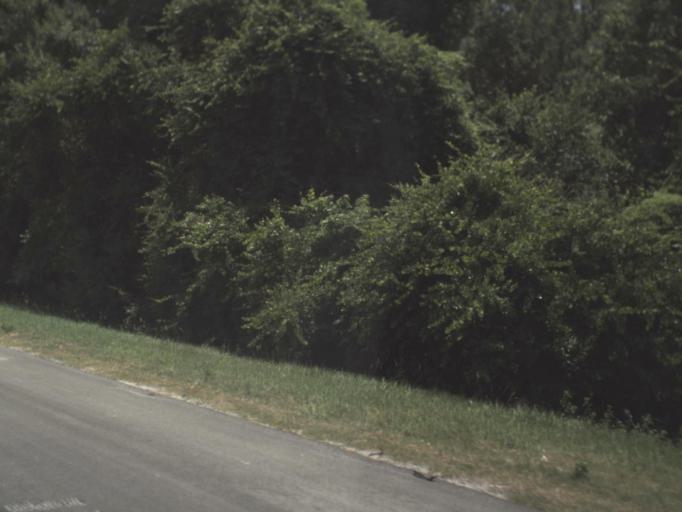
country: US
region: Florida
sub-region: Madison County
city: Madison
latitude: 30.4112
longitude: -83.4234
